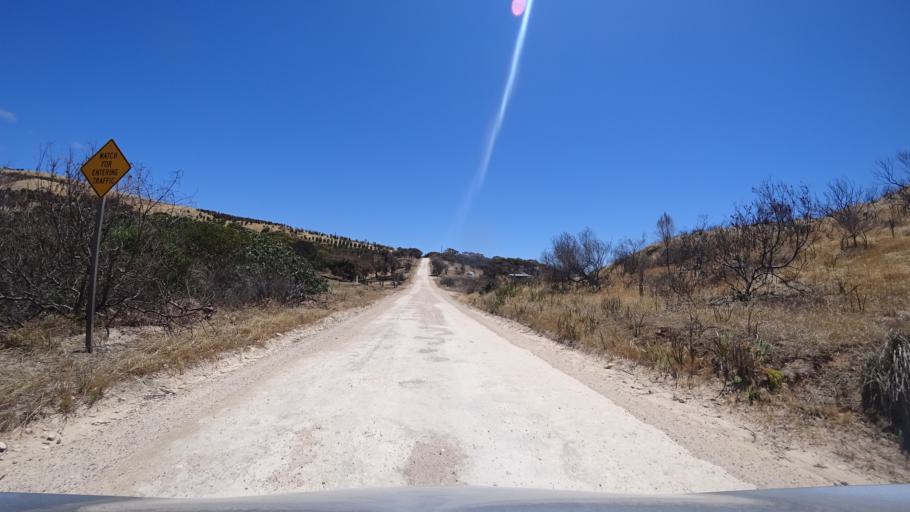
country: AU
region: South Australia
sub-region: Kangaroo Island
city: Kingscote
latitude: -35.6698
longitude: 137.0721
